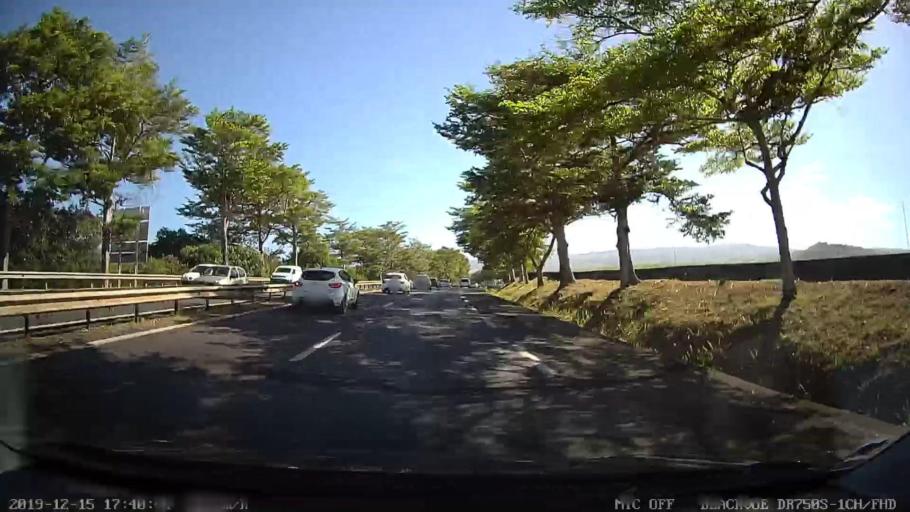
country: RE
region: Reunion
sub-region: Reunion
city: Saint-Pierre
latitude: -21.3165
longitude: 55.4912
